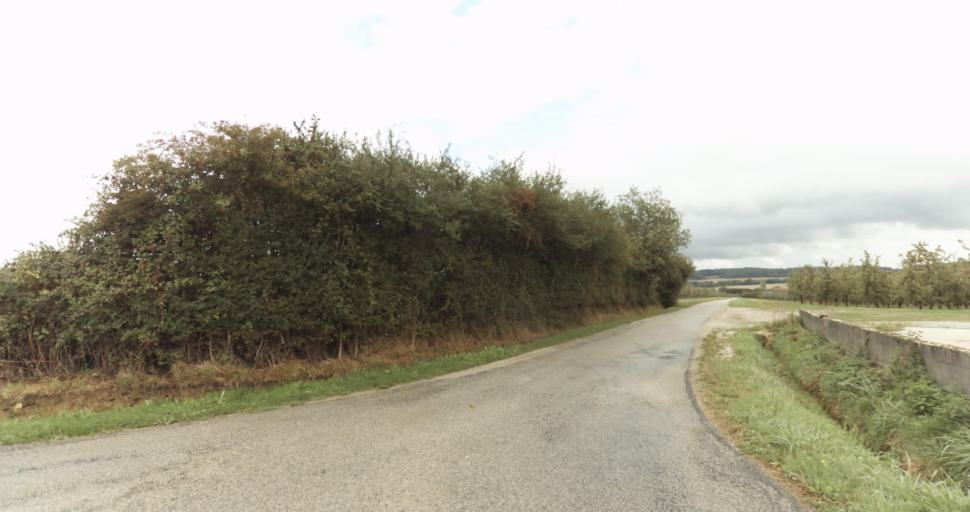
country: FR
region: Lower Normandy
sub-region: Departement de l'Orne
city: Sainte-Gauburge-Sainte-Colombe
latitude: 48.7183
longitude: 0.3912
